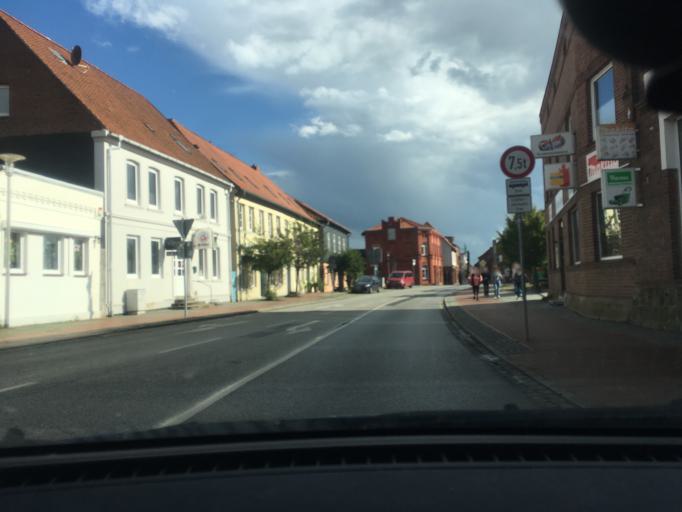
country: DE
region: Mecklenburg-Vorpommern
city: Boizenburg
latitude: 53.3768
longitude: 10.7181
